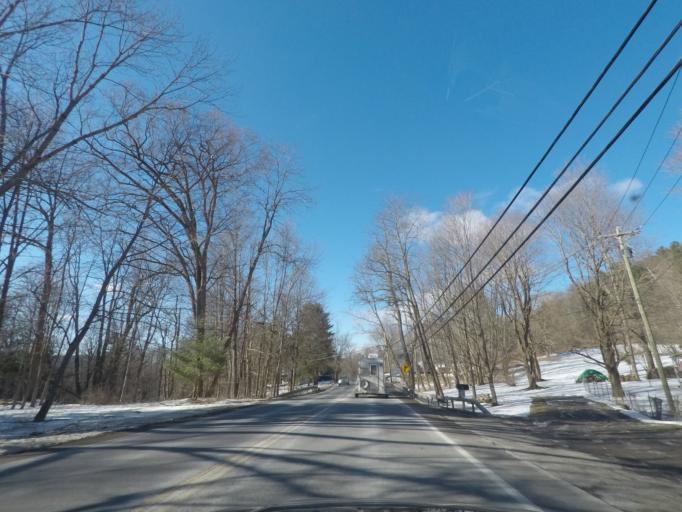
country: US
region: Massachusetts
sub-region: Berkshire County
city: Richmond
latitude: 42.4060
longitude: -73.4298
